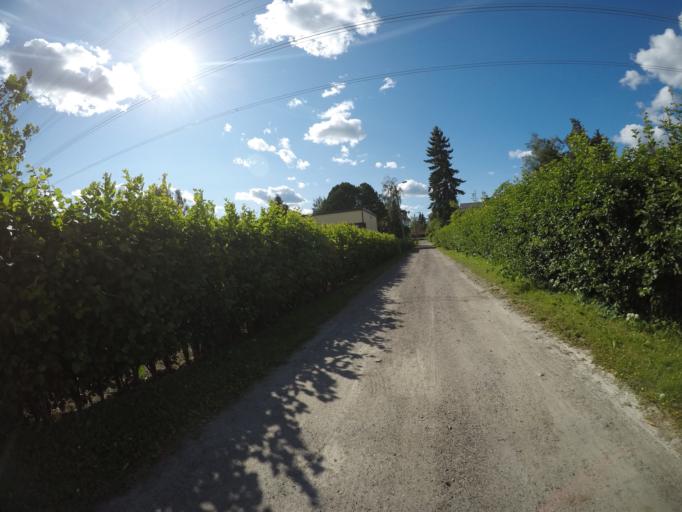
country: FI
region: Haeme
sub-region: Haemeenlinna
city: Haemeenlinna
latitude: 61.0037
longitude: 24.5031
